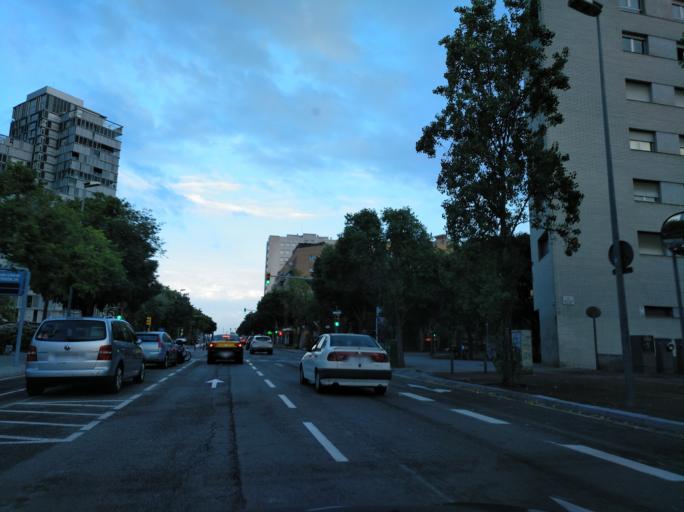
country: ES
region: Catalonia
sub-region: Provincia de Barcelona
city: Sant Marti
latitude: 41.4060
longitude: 2.2128
